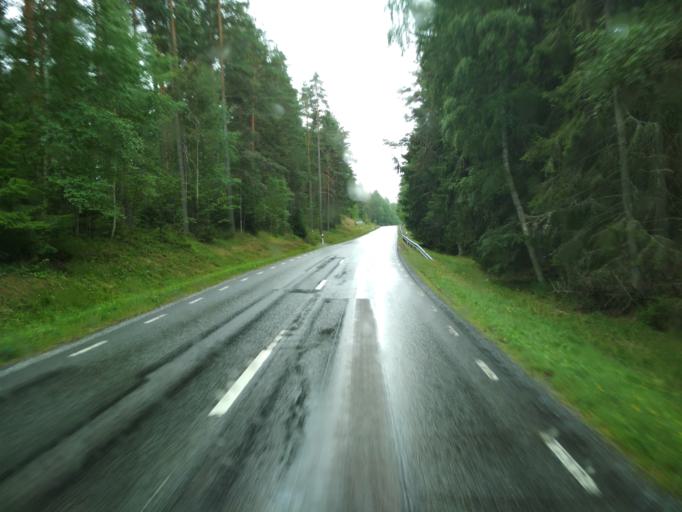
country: SE
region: Vaestmanland
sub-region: Surahammars Kommun
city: Ramnas
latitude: 59.7458
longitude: 16.2053
